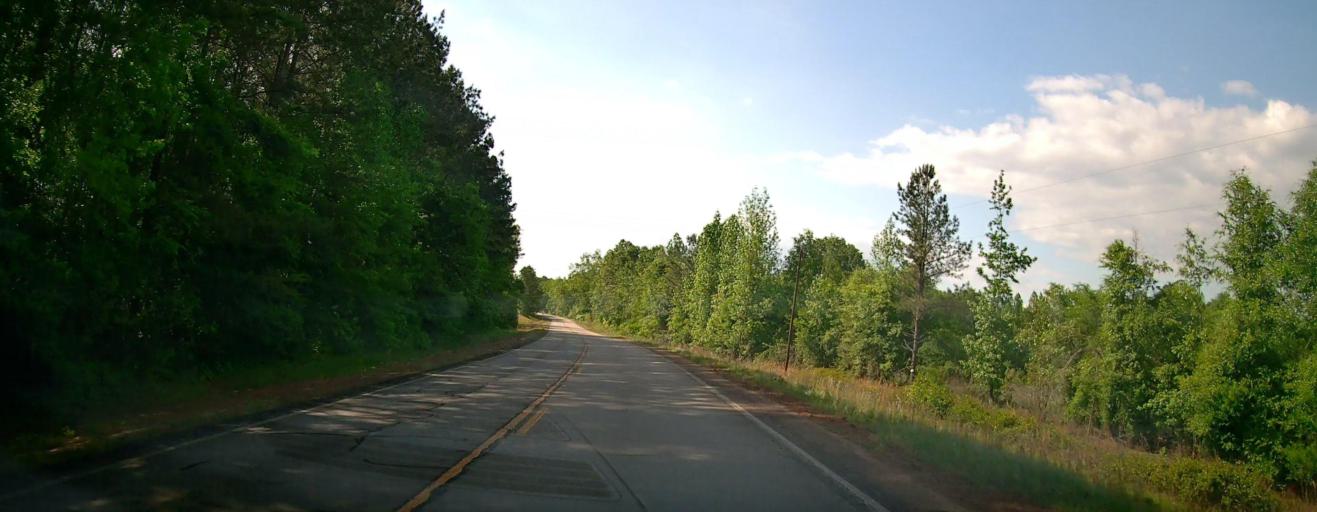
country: US
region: Georgia
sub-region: Washington County
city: Tennille
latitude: 32.9056
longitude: -82.9718
